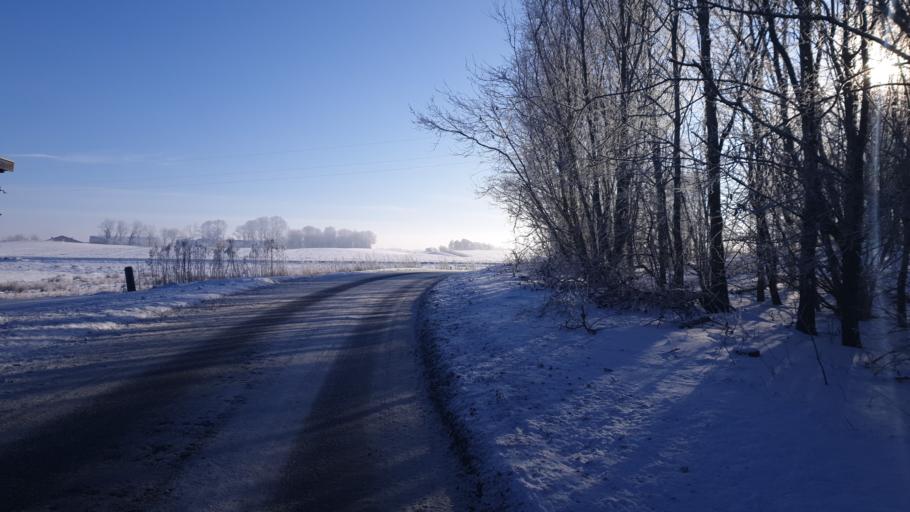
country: DK
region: Central Jutland
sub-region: Hedensted Kommune
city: Hedensted
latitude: 55.8053
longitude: 9.7340
